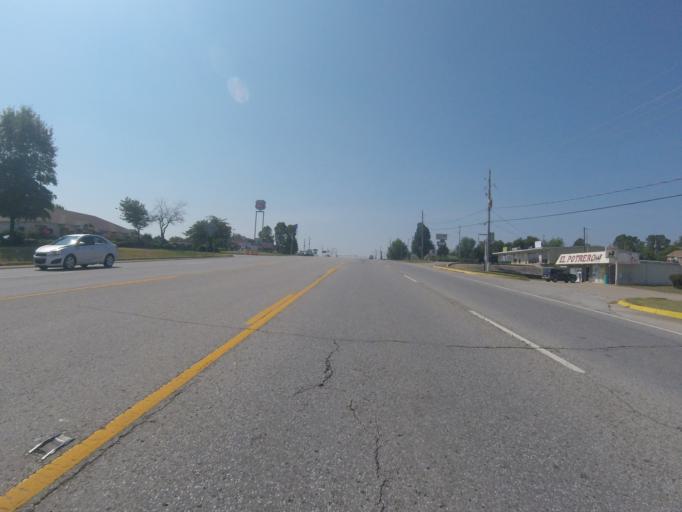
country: US
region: Arkansas
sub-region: Washington County
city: Johnson
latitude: 36.1556
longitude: -94.1439
